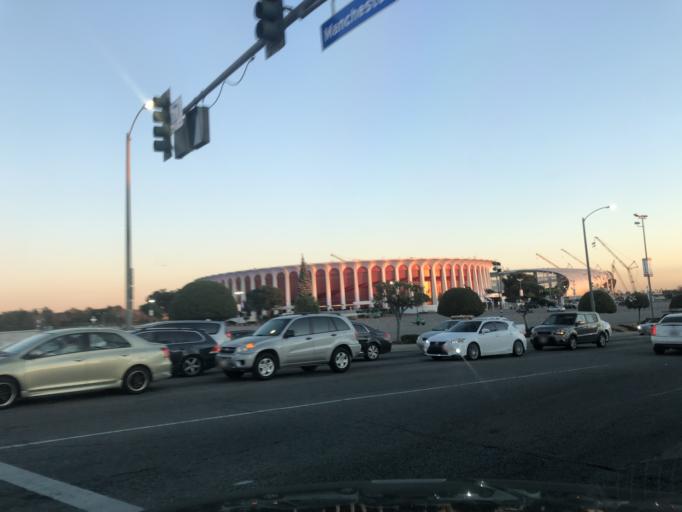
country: US
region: California
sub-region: Los Angeles County
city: Inglewood
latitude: 33.9597
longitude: -118.3441
